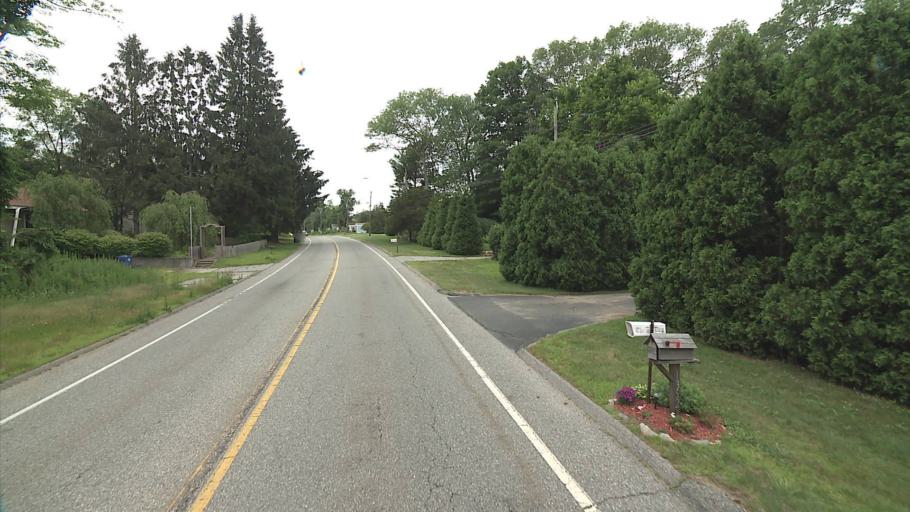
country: US
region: Connecticut
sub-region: New London County
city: Conning Towers-Nautilus Park
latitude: 41.3897
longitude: -72.0277
